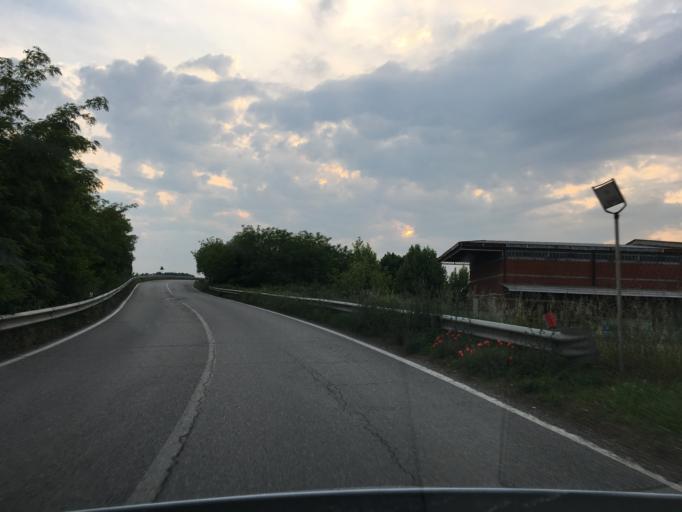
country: IT
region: Lombardy
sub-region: Provincia di Brescia
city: Alfianello
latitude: 45.2696
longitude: 10.1314
